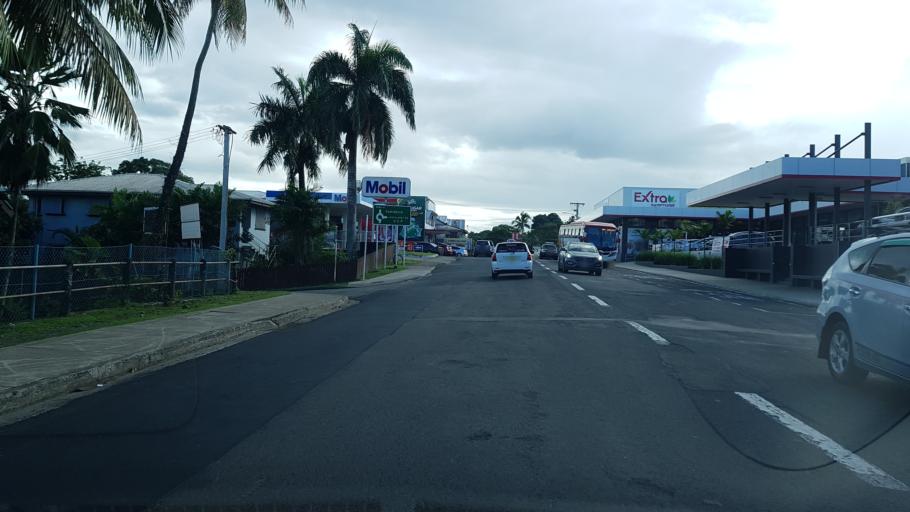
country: FJ
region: Central
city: Suva
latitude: -18.1450
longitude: 178.4348
